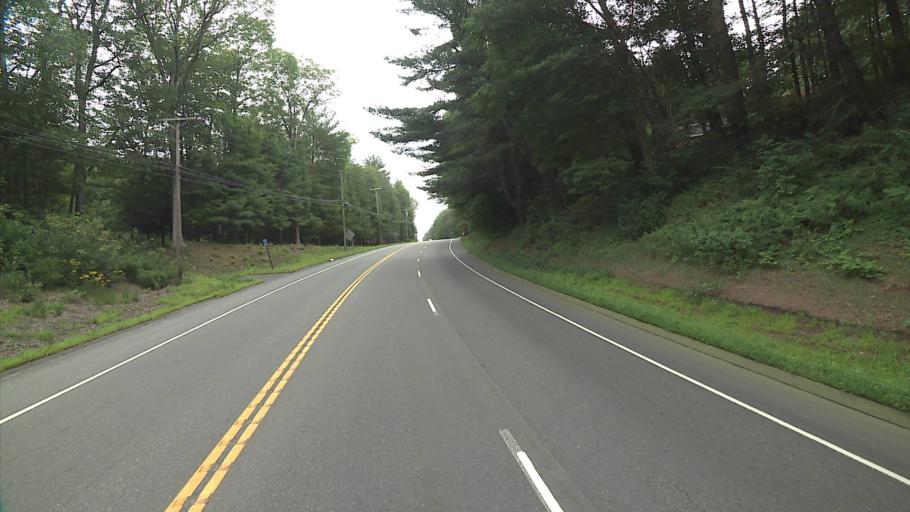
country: US
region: Connecticut
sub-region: Tolland County
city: Stafford Springs
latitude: 41.8825
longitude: -72.2950
